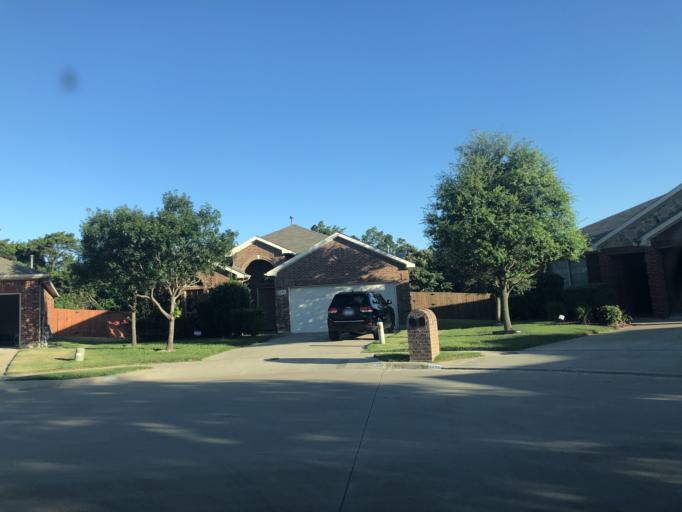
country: US
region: Texas
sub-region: Dallas County
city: Duncanville
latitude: 32.6521
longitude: -96.9515
